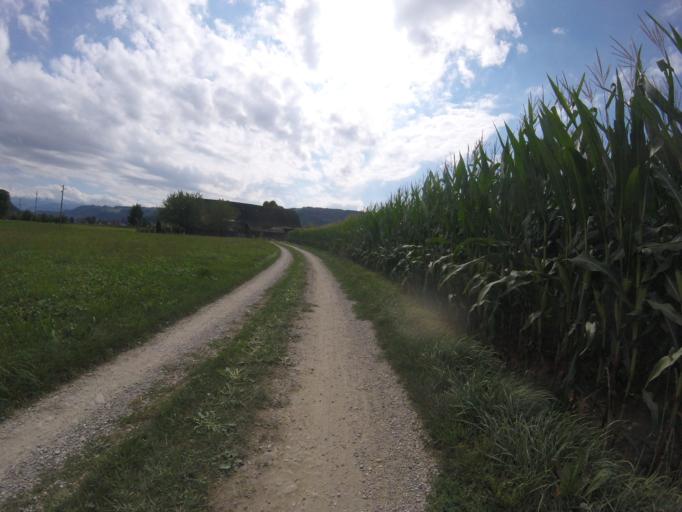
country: CH
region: Bern
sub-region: Bern-Mittelland District
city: Belp
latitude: 46.9025
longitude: 7.5118
